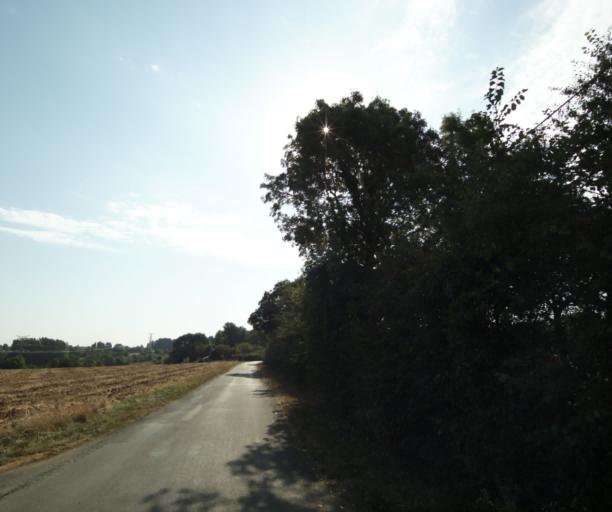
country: FR
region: Poitou-Charentes
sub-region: Departement de la Charente-Maritime
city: Tonnay-Charente
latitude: 45.9660
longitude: -0.8645
